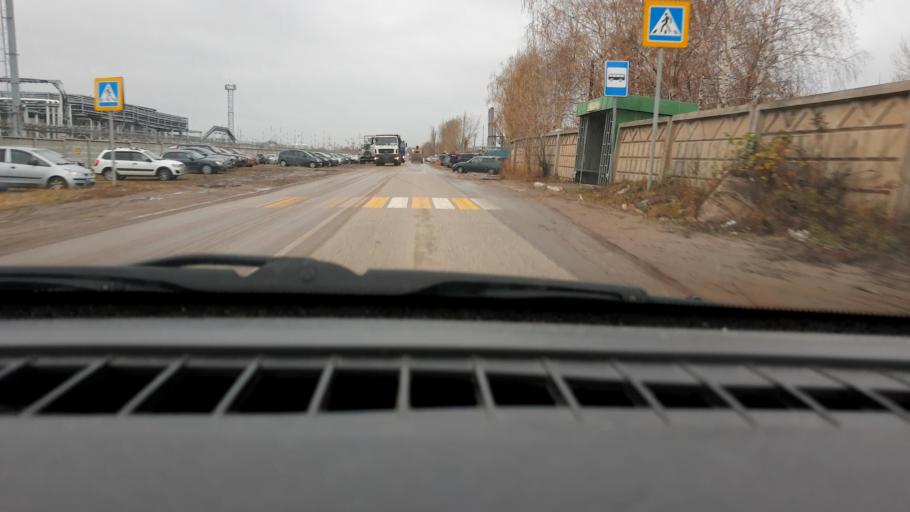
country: RU
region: Nizjnij Novgorod
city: Kstovo
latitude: 56.1215
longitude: 44.1365
